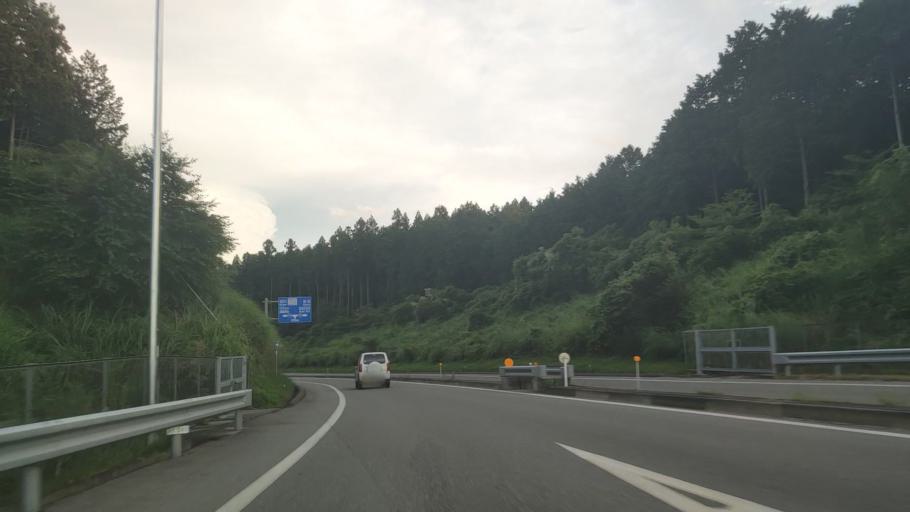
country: JP
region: Tochigi
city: Imaichi
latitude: 36.6993
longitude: 139.7148
